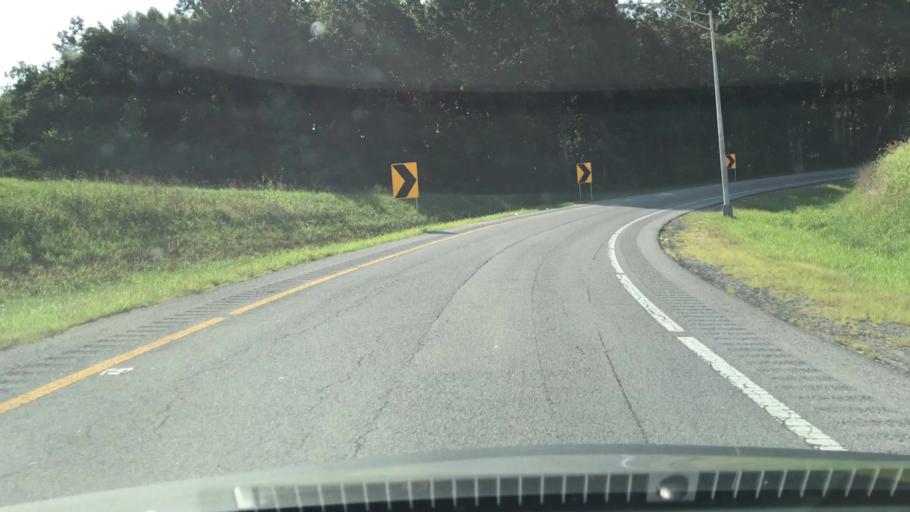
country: US
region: Kentucky
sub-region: Metcalfe County
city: Edmonton
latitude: 36.9962
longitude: -85.6571
